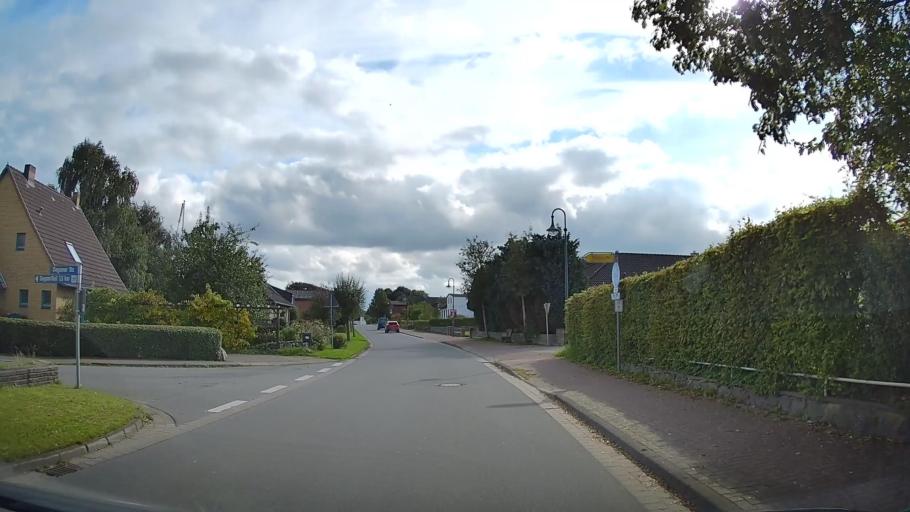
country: DE
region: Schleswig-Holstein
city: Ringsberg
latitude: 54.8090
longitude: 9.5977
